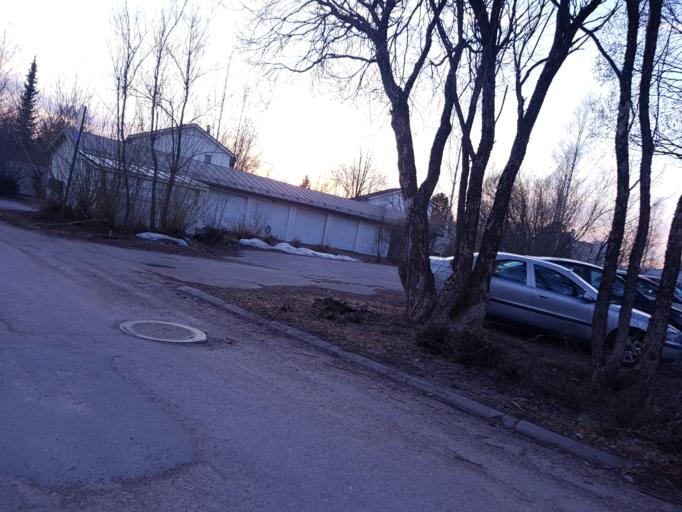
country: FI
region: Uusimaa
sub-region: Helsinki
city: Helsinki
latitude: 60.2578
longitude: 24.9479
